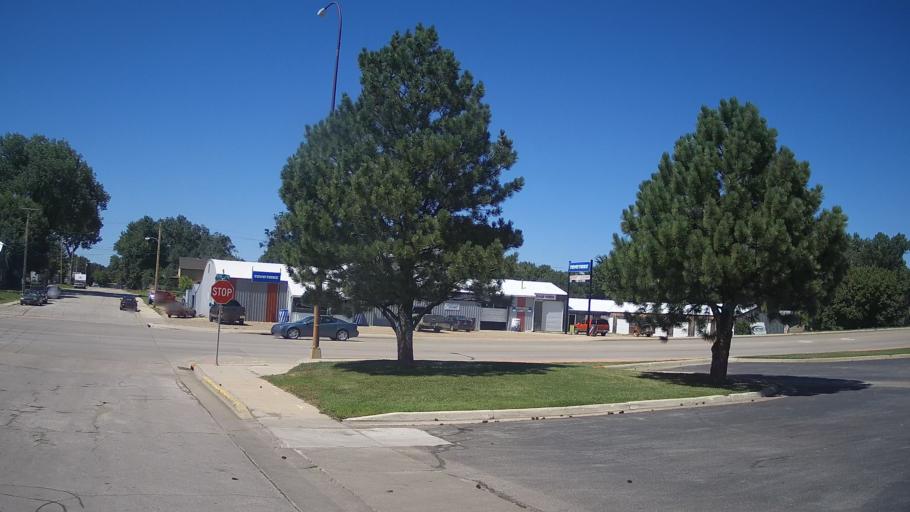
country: US
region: South Dakota
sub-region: Butte County
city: Belle Fourche
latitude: 44.6737
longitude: -103.8531
